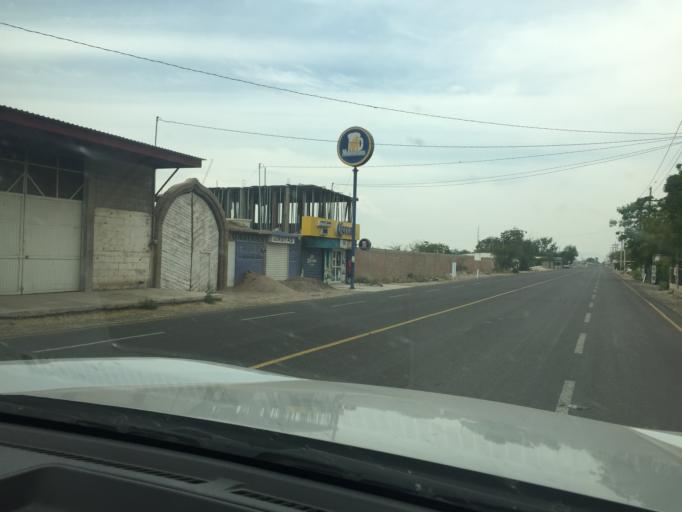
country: MX
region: Durango
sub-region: Gomez Palacio
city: San Jose de Vinedo
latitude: 25.6825
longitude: -103.4443
